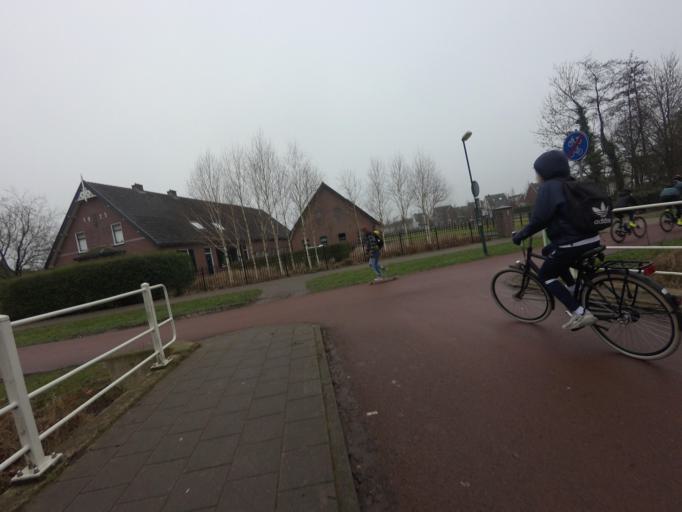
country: NL
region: Utrecht
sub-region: Gemeente Houten
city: Houten
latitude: 52.0173
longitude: 5.1705
